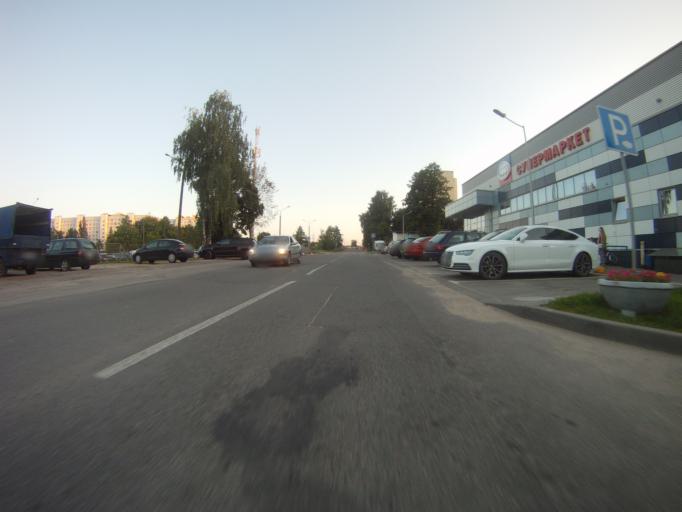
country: BY
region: Minsk
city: Novoye Medvezhino
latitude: 53.9260
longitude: 27.4756
